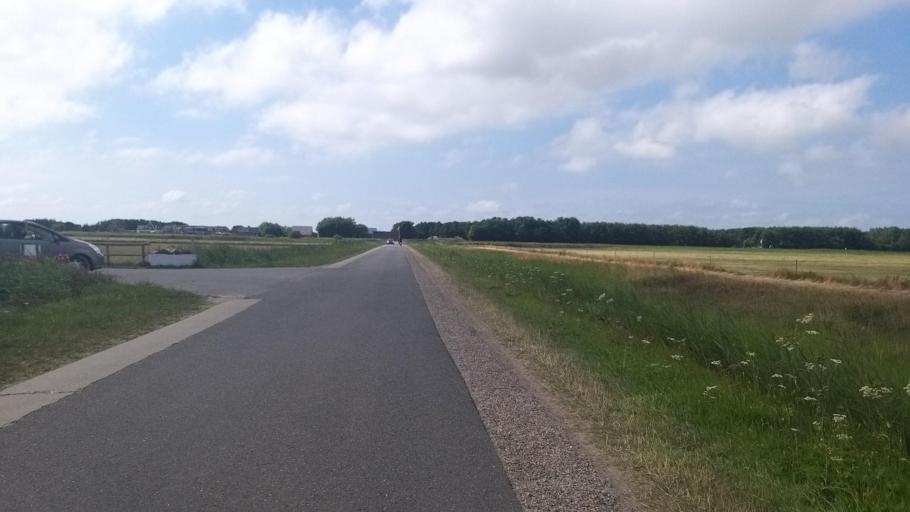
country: NL
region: North Holland
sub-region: Gemeente Texel
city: Den Burg
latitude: 53.1449
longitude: 4.8662
